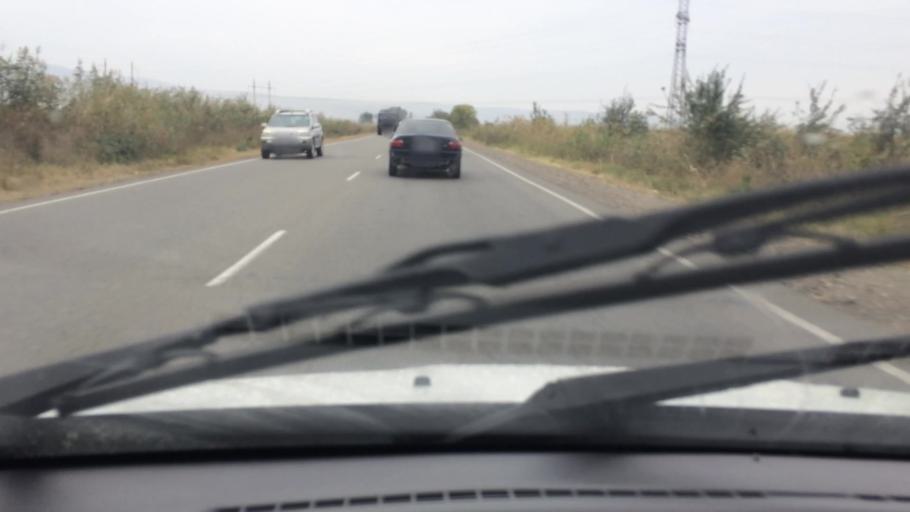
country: GE
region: Kvemo Kartli
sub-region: Marneuli
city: Marneuli
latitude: 41.5404
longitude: 44.7768
